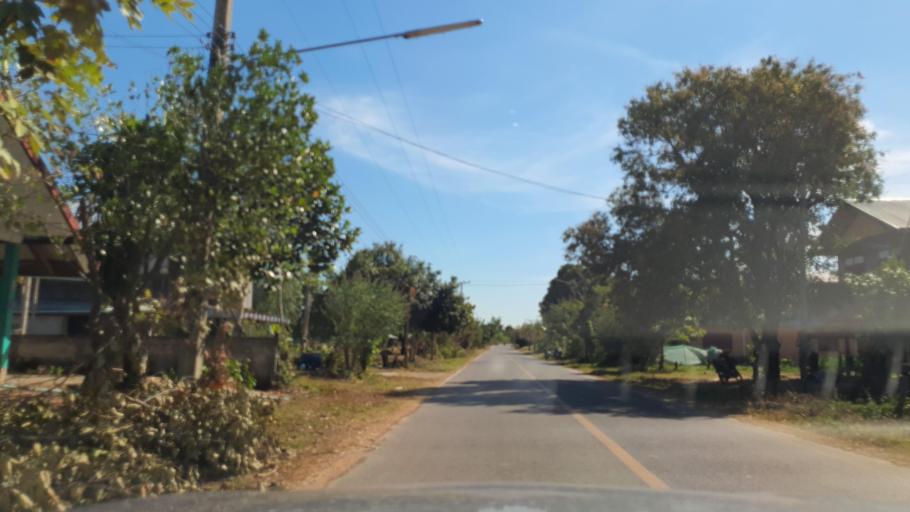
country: TH
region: Kalasin
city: Khao Wong
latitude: 16.7145
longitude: 104.1145
